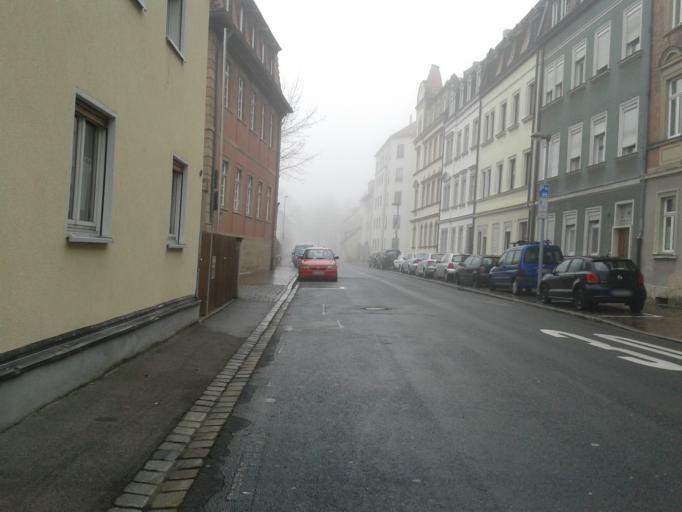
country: DE
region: Bavaria
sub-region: Upper Franconia
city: Bamberg
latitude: 49.8943
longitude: 10.9014
